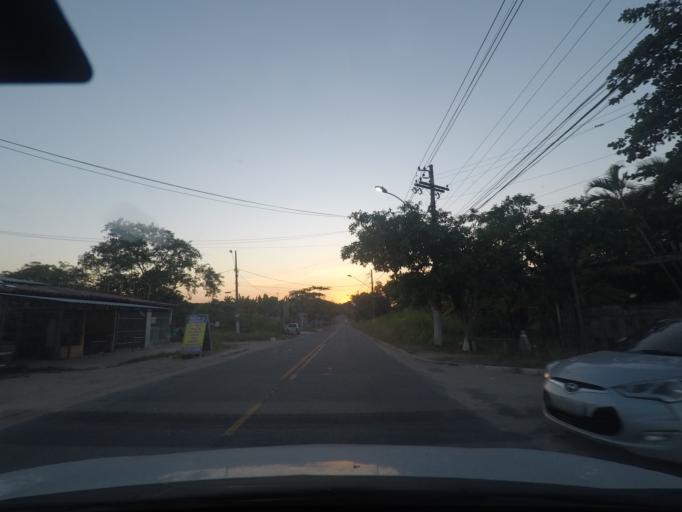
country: BR
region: Rio de Janeiro
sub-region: Sao Goncalo
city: Sao Goncalo
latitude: -22.9478
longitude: -42.9673
